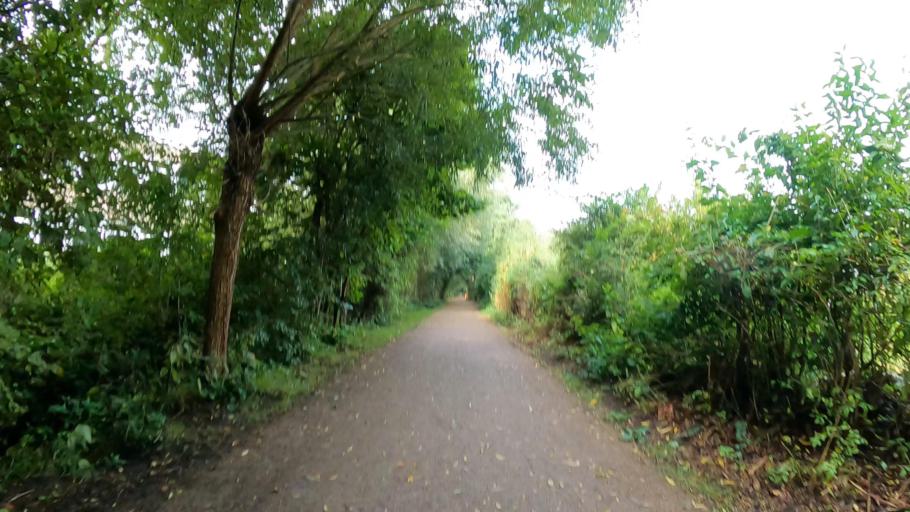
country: DE
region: Hamburg
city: Eidelstedt
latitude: 53.5973
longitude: 9.8943
